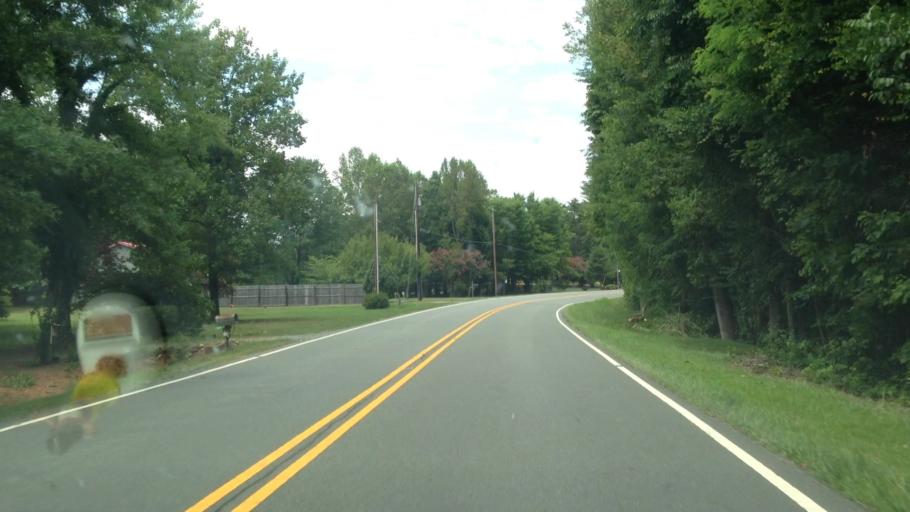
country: US
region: North Carolina
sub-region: Stokes County
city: Danbury
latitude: 36.3981
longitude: -80.0950
